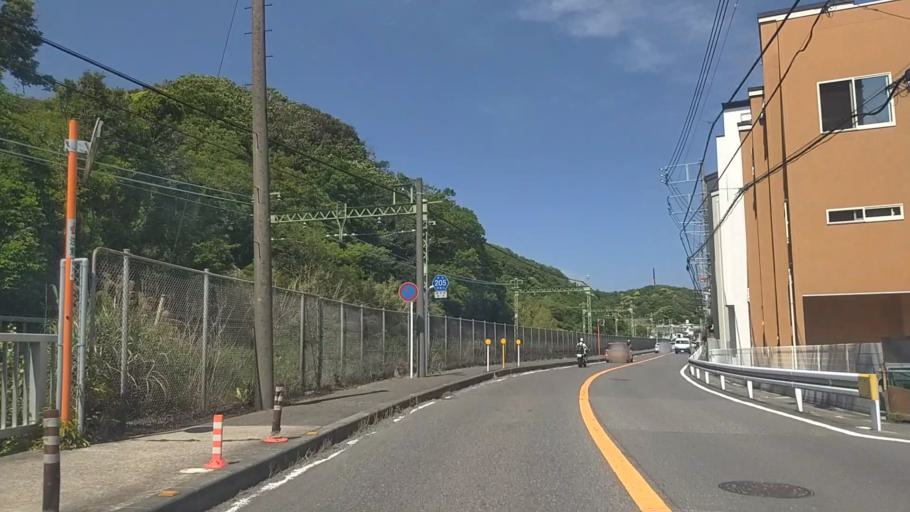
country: JP
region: Kanagawa
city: Zushi
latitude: 35.3079
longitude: 139.5955
